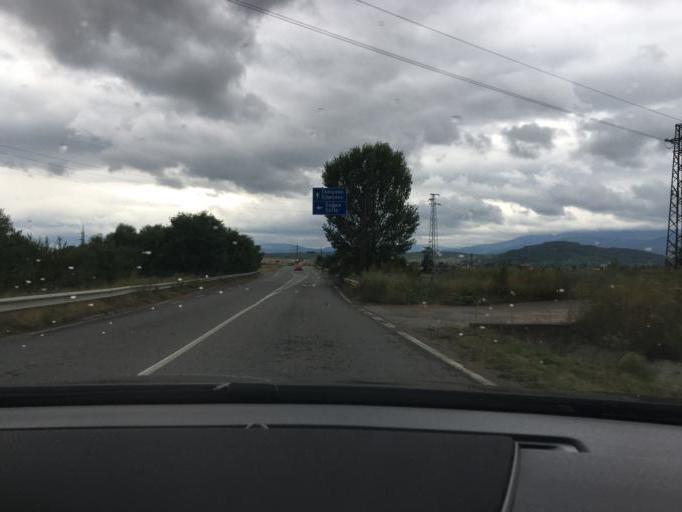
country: BG
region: Kyustendil
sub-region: Obshtina Kyustendil
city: Kyustendil
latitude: 42.2921
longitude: 22.7205
